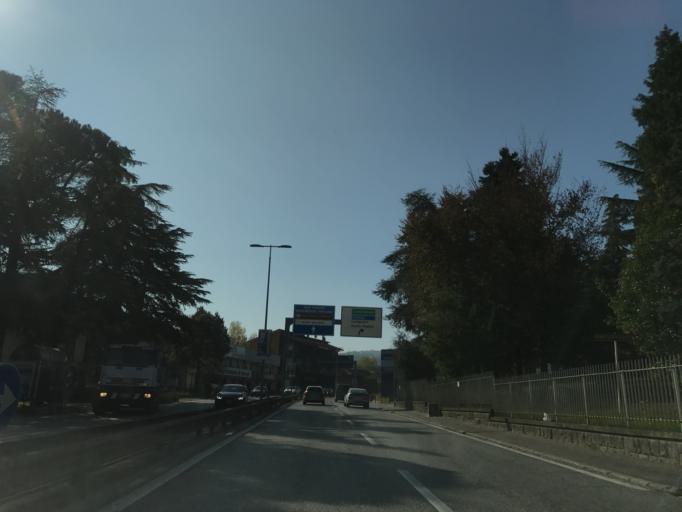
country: SM
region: Serravalle
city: Serravalle
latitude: 43.9755
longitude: 12.4863
